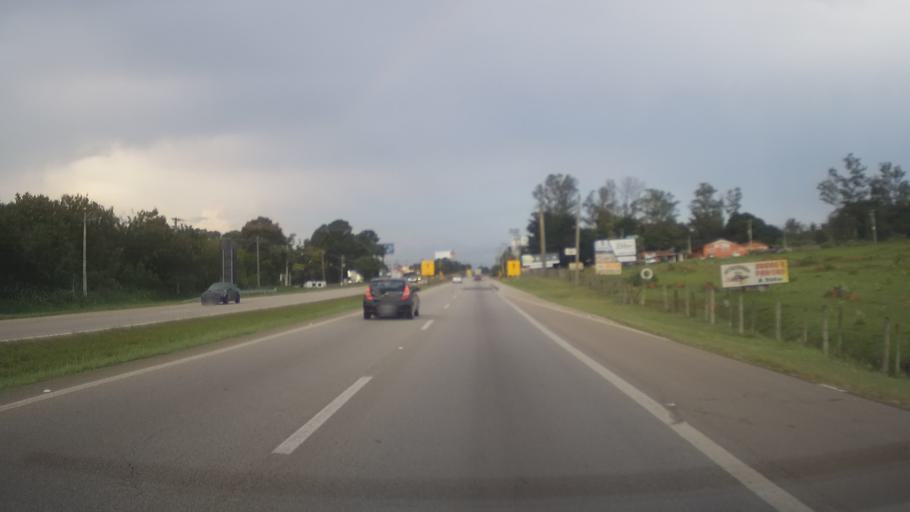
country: BR
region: Sao Paulo
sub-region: Itupeva
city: Itupeva
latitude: -23.1938
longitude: -46.9923
